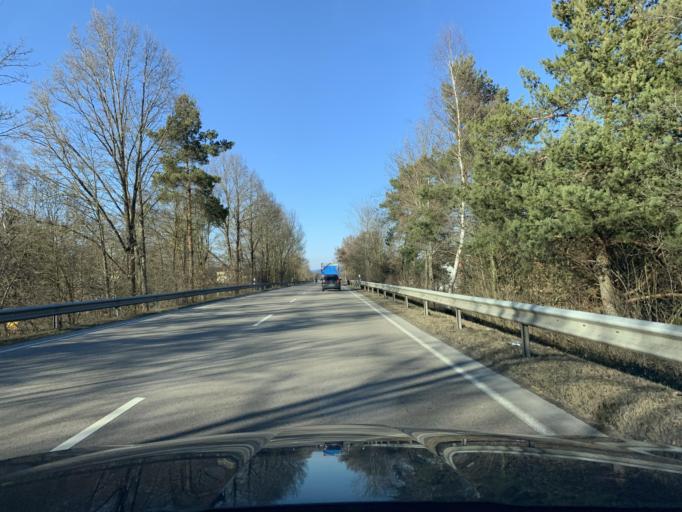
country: DE
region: Bavaria
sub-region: Upper Palatinate
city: Pemfling
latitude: 49.3036
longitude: 12.6297
